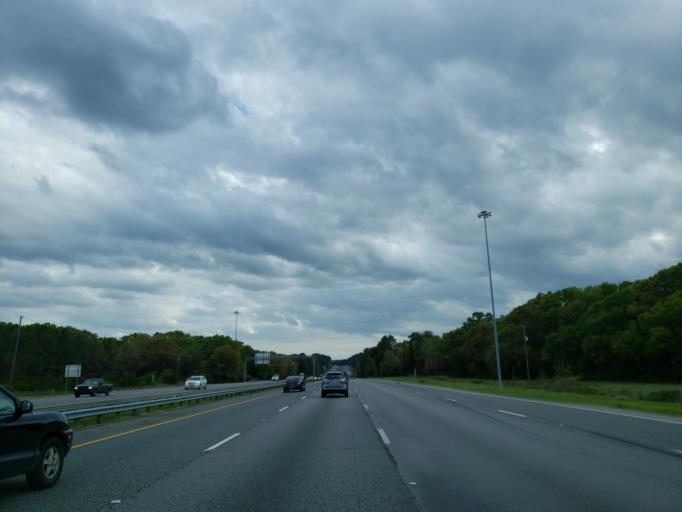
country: US
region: Georgia
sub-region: Houston County
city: Perry
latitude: 32.4285
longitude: -83.7582
